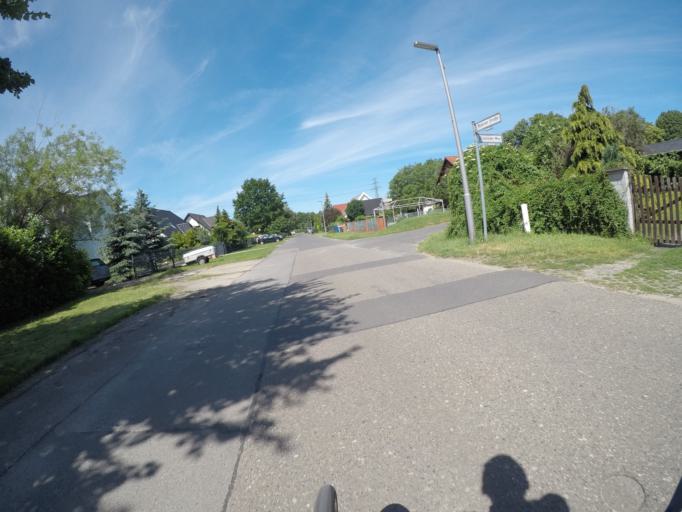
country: DE
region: Berlin
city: Biesdorf
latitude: 52.5067
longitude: 13.5448
